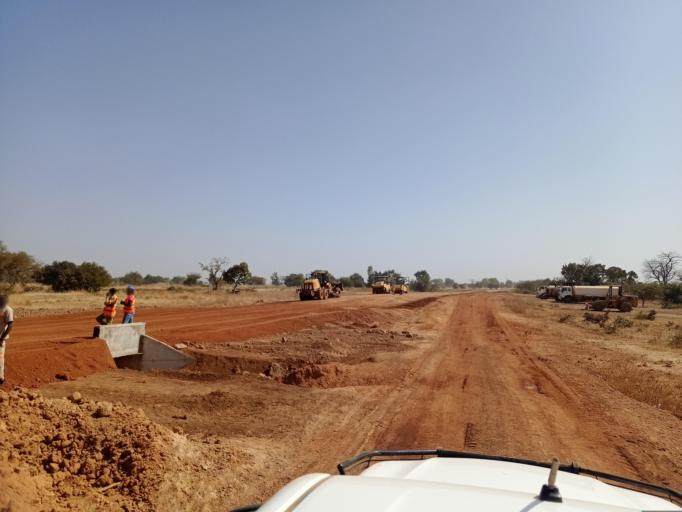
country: BF
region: Centre-Est
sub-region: Province du Boulgou
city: Garango
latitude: 11.5022
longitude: -0.5007
